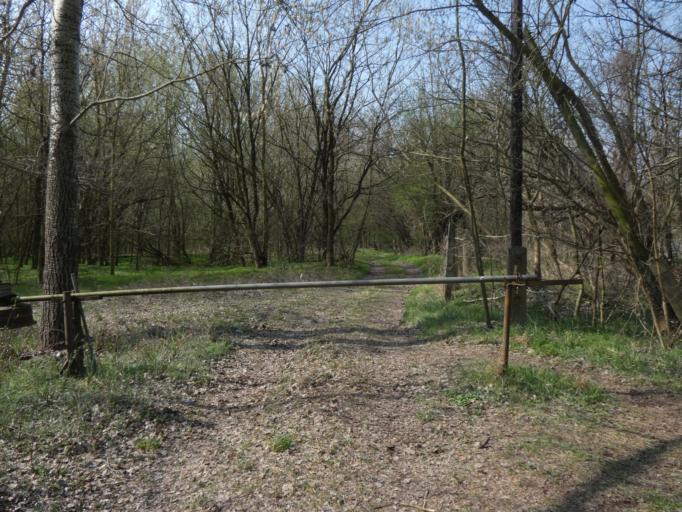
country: HU
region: Pest
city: Ocsa
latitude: 47.2559
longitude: 19.2330
